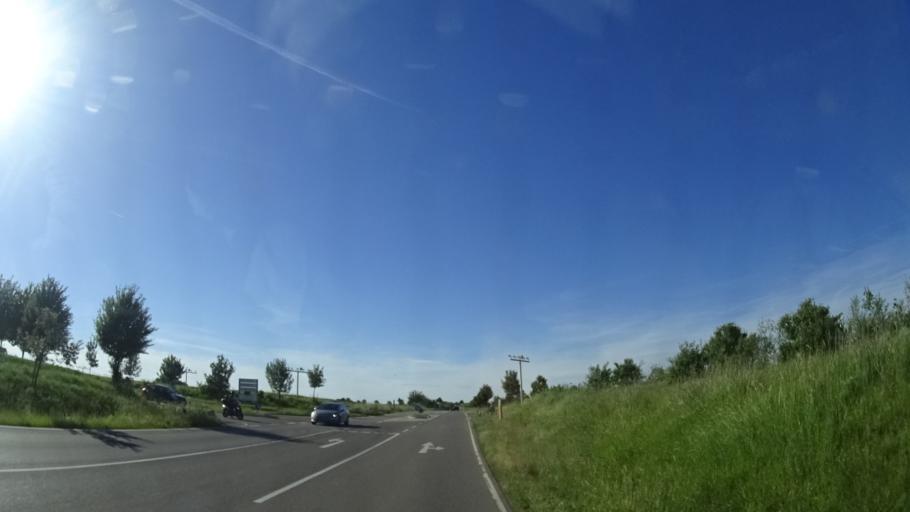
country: DE
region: Baden-Wuerttemberg
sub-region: Regierungsbezirk Stuttgart
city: Schwaebisch Hall
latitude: 49.1193
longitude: 9.7688
